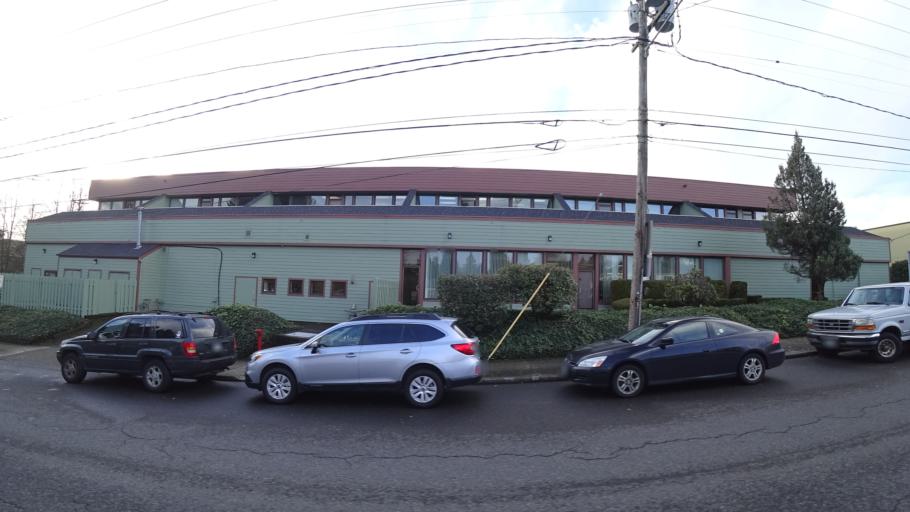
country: US
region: Oregon
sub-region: Multnomah County
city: Lents
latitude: 45.5177
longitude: -122.5539
